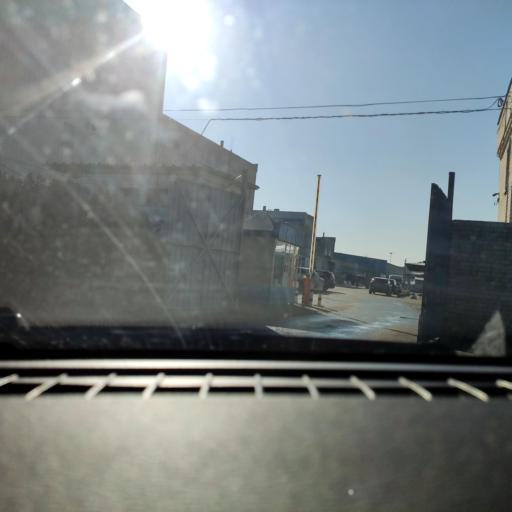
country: RU
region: Voronezj
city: Somovo
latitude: 51.6825
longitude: 39.3006
